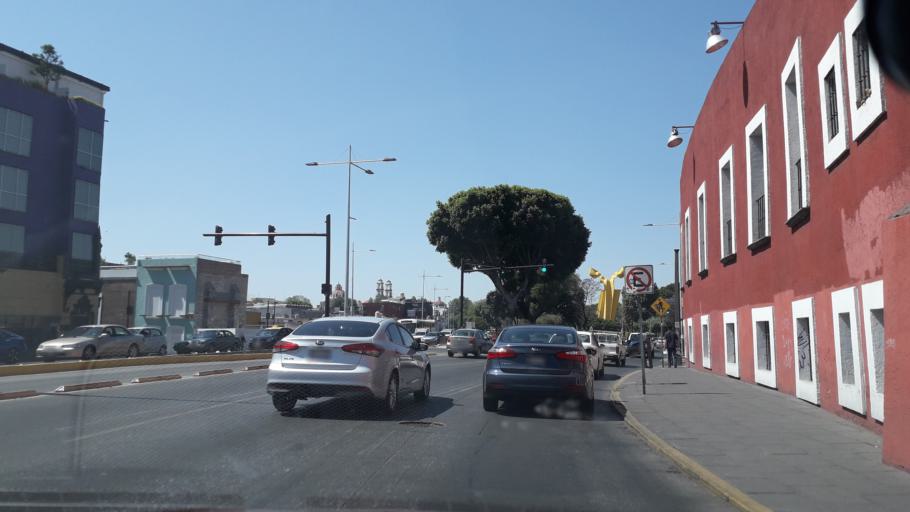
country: MX
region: Puebla
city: Puebla
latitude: 19.0427
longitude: -98.1924
